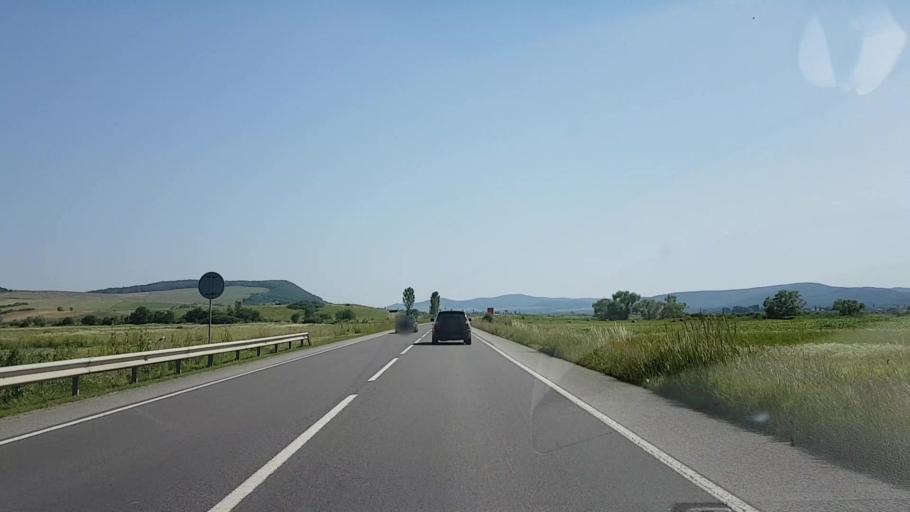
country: RO
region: Bistrita-Nasaud
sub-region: Comuna Sintereag
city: Sintereag
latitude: 47.1714
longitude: 24.3081
